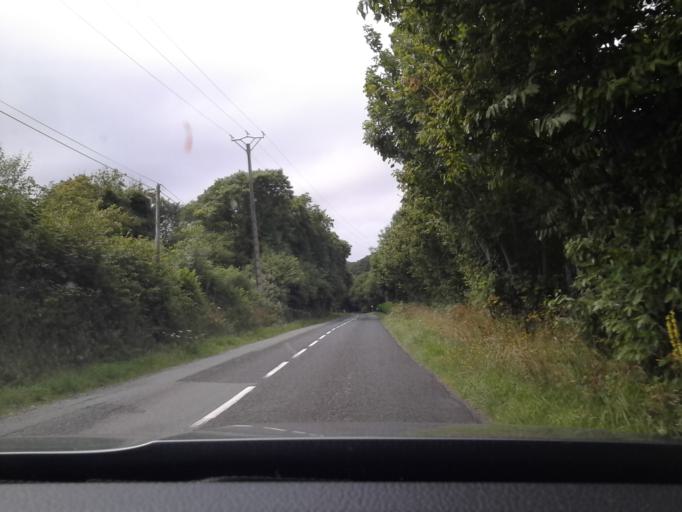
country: FR
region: Lower Normandy
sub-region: Departement de la Manche
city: Beaumont-Hague
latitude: 49.6698
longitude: -1.8177
